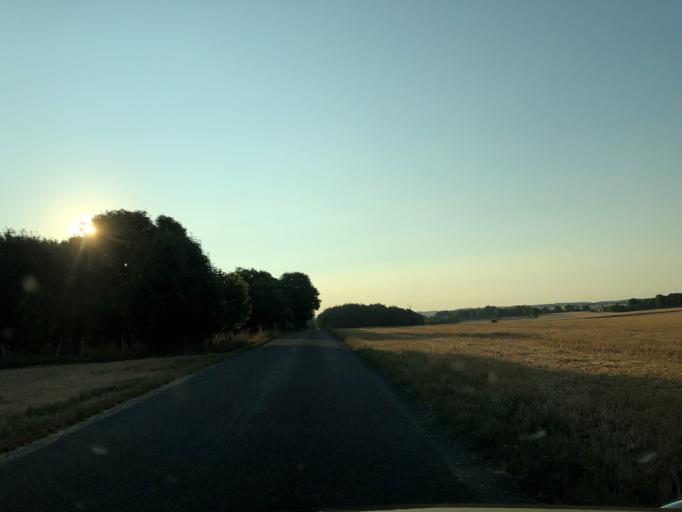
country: DK
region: Central Jutland
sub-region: Skanderborg Kommune
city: Skanderborg
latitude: 56.0877
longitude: 9.8889
